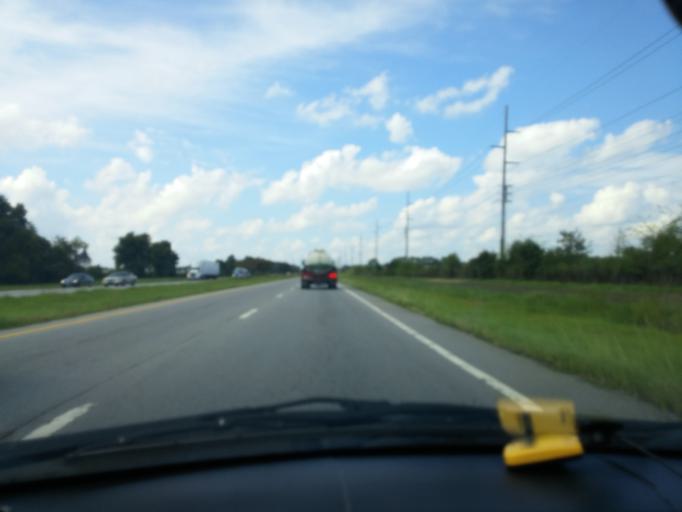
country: US
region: North Carolina
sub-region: Pitt County
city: Greenville
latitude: 35.6444
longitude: -77.3388
